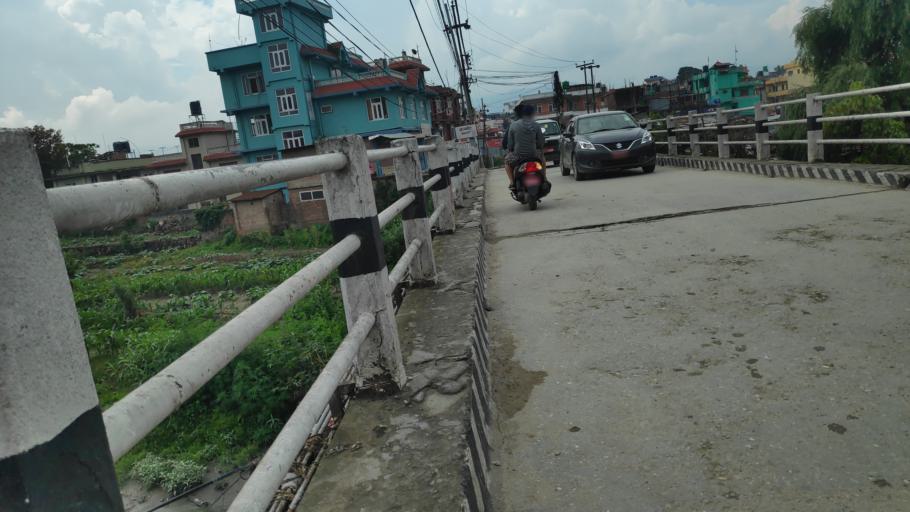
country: NP
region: Central Region
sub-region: Bagmati Zone
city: Patan
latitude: 27.6730
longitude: 85.3646
